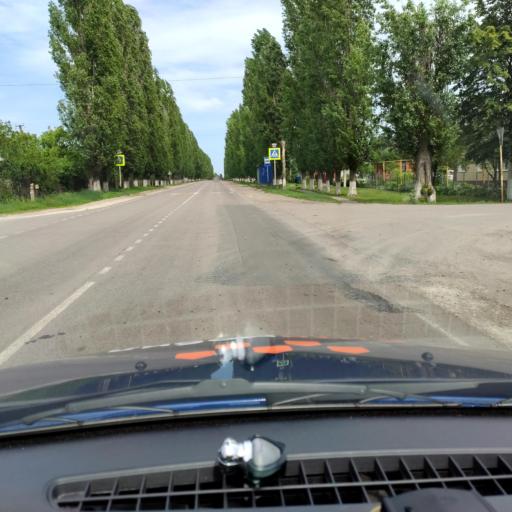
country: RU
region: Voronezj
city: Maslovka
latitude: 51.5352
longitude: 39.3258
